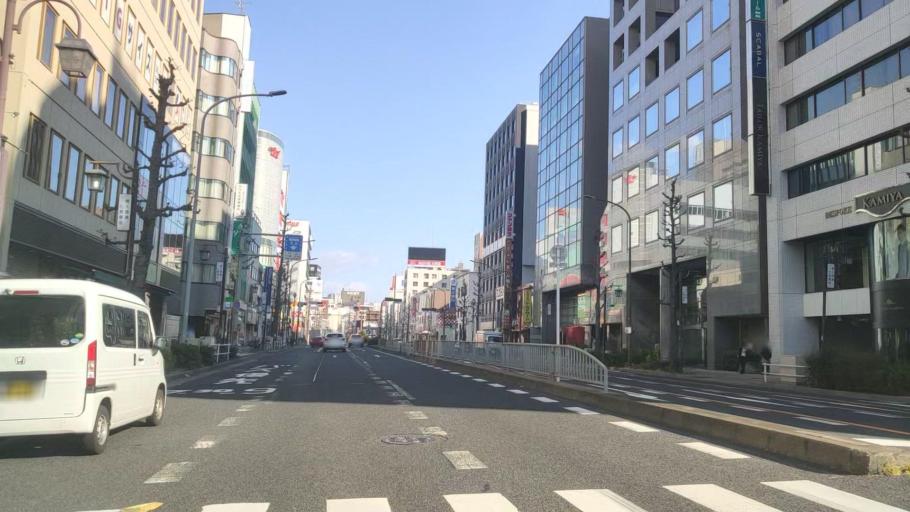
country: JP
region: Aichi
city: Nagoya-shi
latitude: 35.1576
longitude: 136.9059
